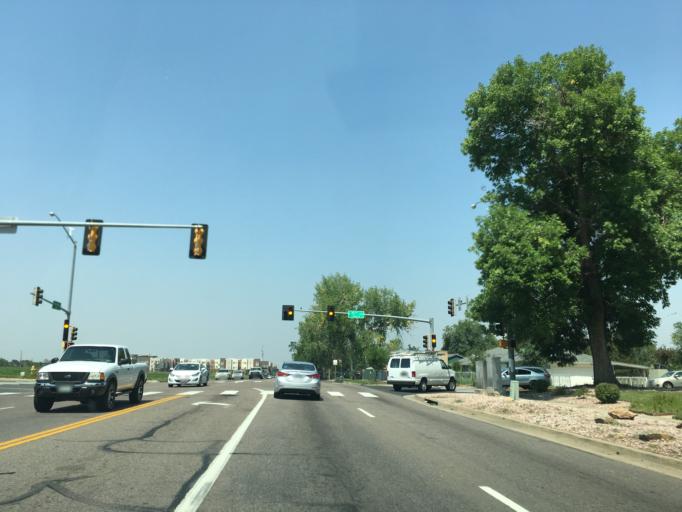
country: US
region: Colorado
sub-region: Adams County
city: Aurora
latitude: 39.7325
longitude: -104.8472
